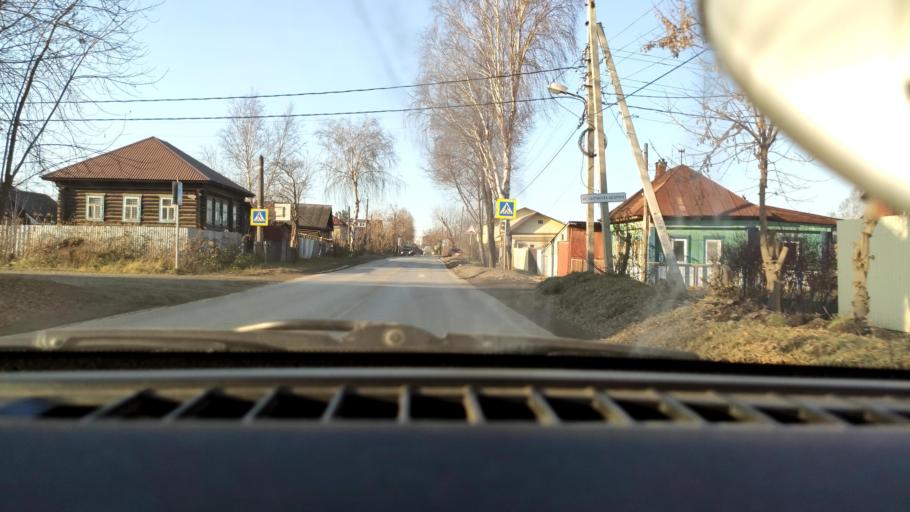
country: RU
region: Perm
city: Perm
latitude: 58.0150
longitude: 56.3173
